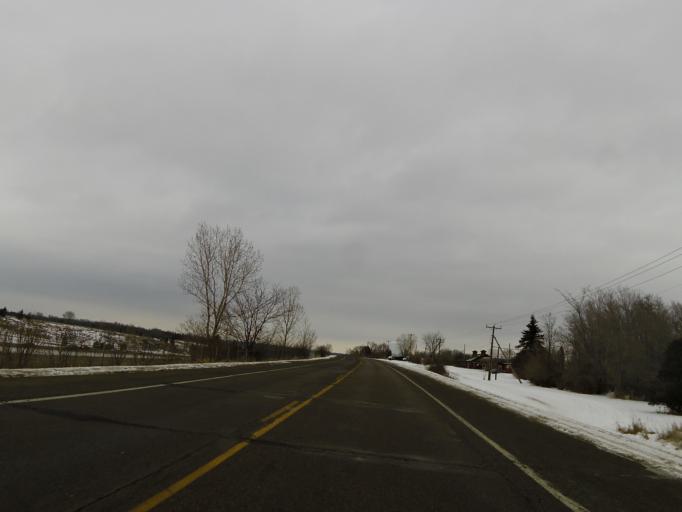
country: US
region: Minnesota
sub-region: Washington County
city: Lakeland
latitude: 44.9569
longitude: -92.7877
